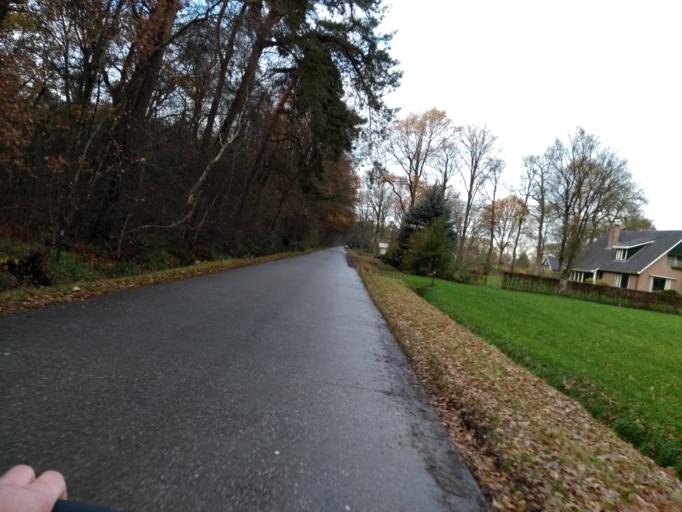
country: NL
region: Overijssel
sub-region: Gemeente Almelo
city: Almelo
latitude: 52.3629
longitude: 6.7177
